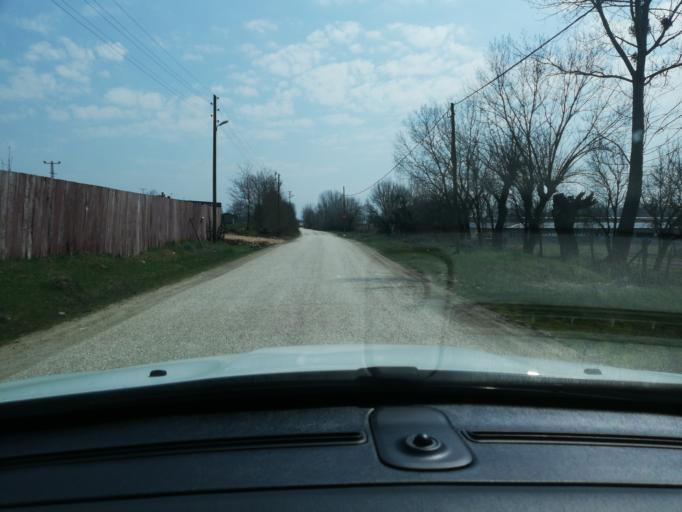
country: TR
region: Kastamonu
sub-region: Cide
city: Kastamonu
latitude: 41.4586
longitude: 33.7638
